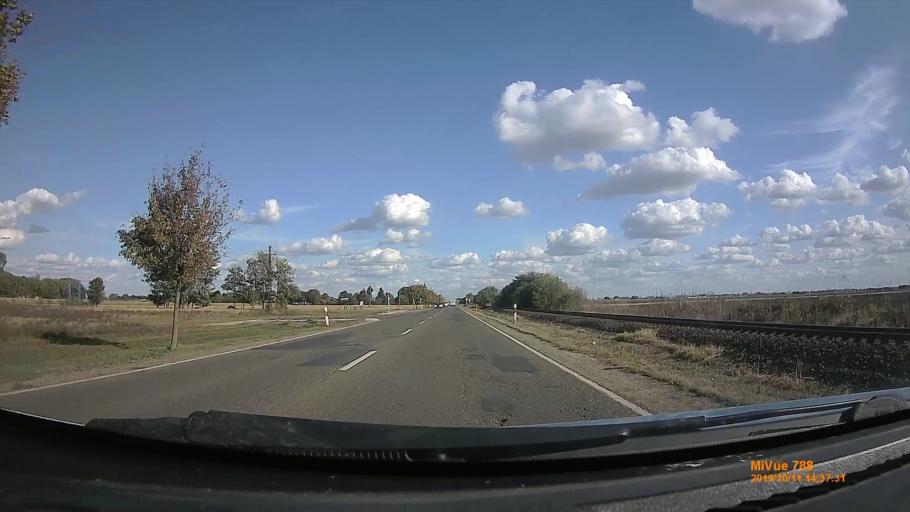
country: HU
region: Hajdu-Bihar
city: Ebes
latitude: 47.5537
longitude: 21.5277
